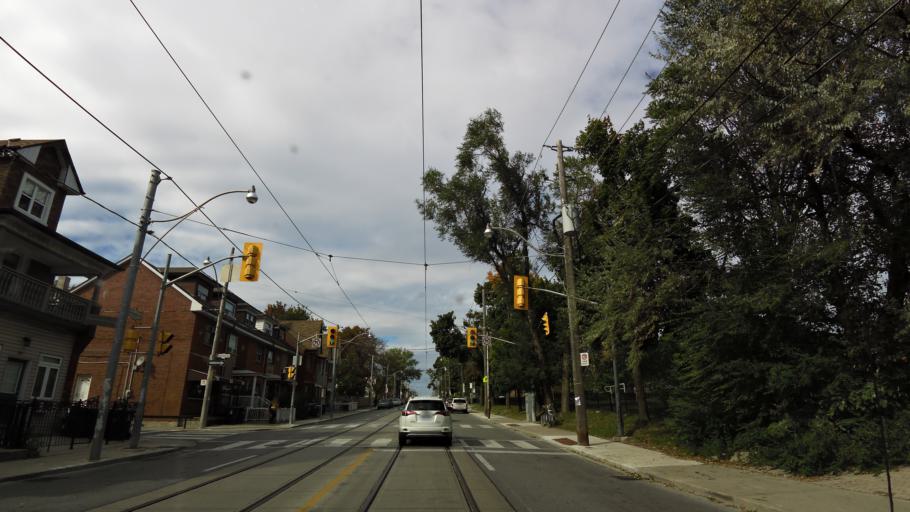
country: CA
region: Ontario
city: Toronto
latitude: 43.6518
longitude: -79.4217
